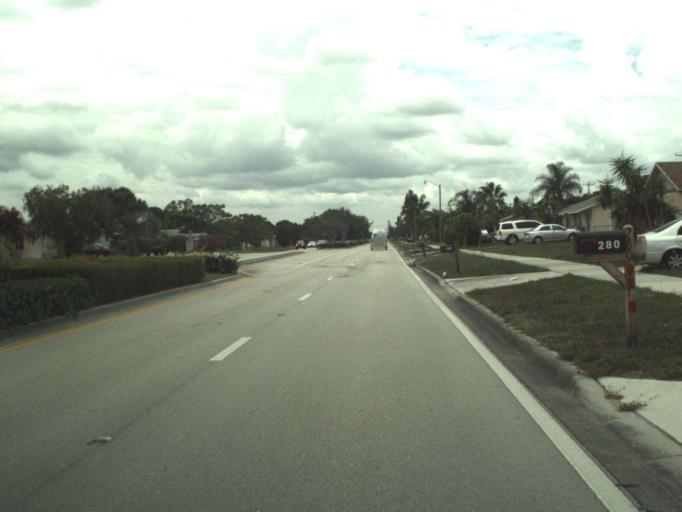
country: US
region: Florida
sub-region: Saint Lucie County
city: River Park
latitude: 27.3231
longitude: -80.3497
